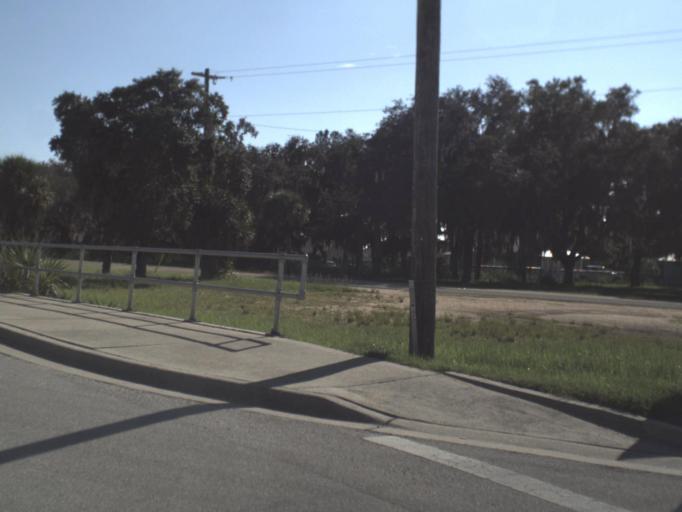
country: US
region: Florida
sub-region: Sarasota County
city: Englewood
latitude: 26.9477
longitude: -82.3533
